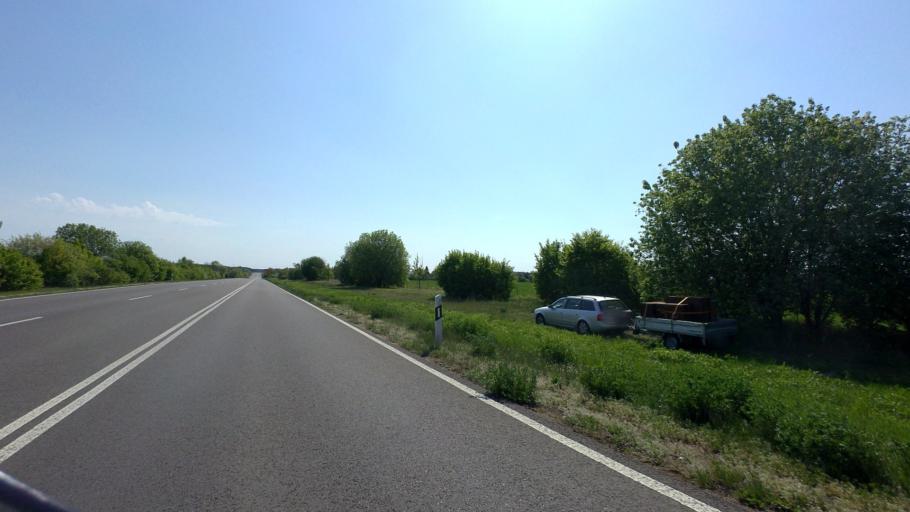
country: DE
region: Brandenburg
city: Beeskow
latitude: 52.1757
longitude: 14.2167
